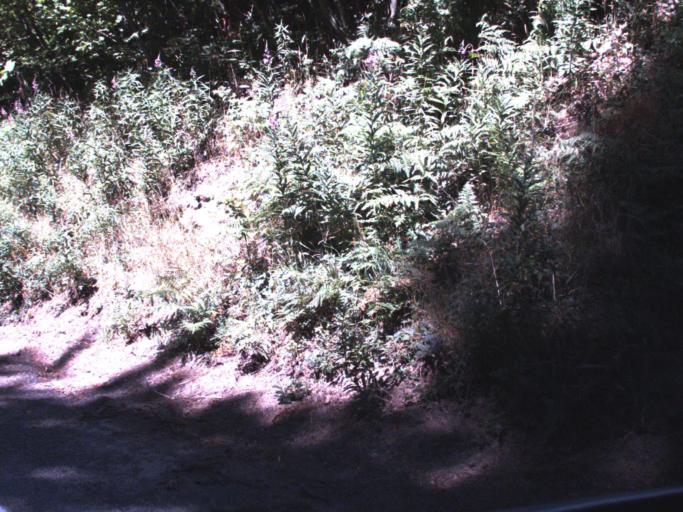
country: US
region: Washington
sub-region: King County
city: Enumclaw
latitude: 47.1690
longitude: -121.8089
